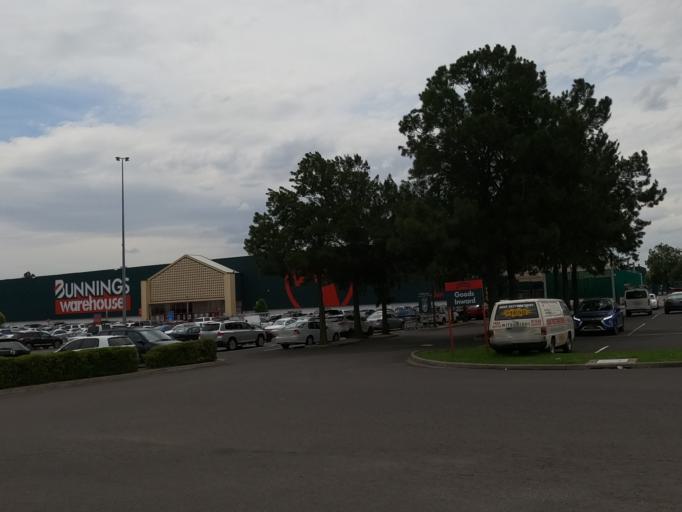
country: AU
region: Victoria
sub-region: Hume
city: Broadmeadows
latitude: -37.6767
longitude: 144.9218
